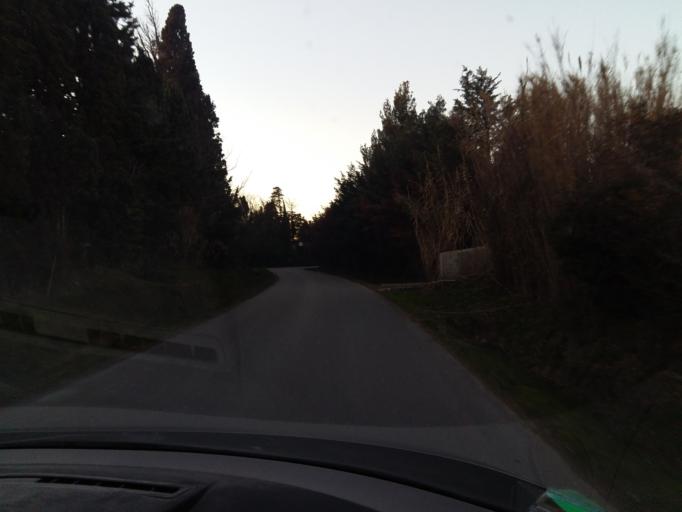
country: FR
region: Provence-Alpes-Cote d'Azur
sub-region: Departement des Bouches-du-Rhone
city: Graveson
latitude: 43.8432
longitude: 4.7771
